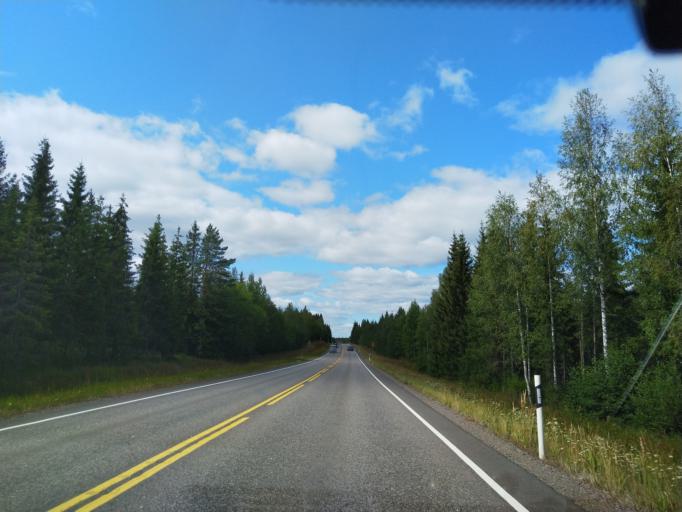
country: FI
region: Haeme
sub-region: Haemeenlinna
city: Renko
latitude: 60.7653
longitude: 24.2583
